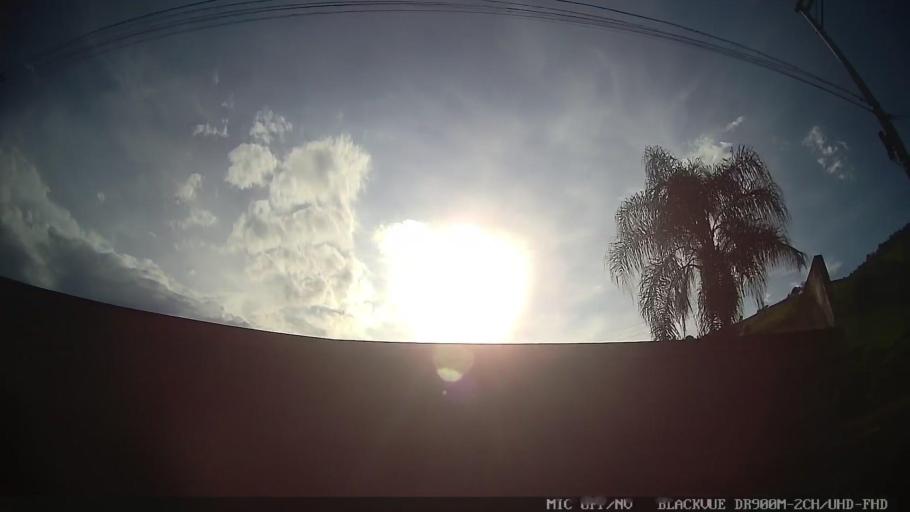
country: BR
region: Sao Paulo
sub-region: Amparo
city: Amparo
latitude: -22.6888
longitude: -46.6910
